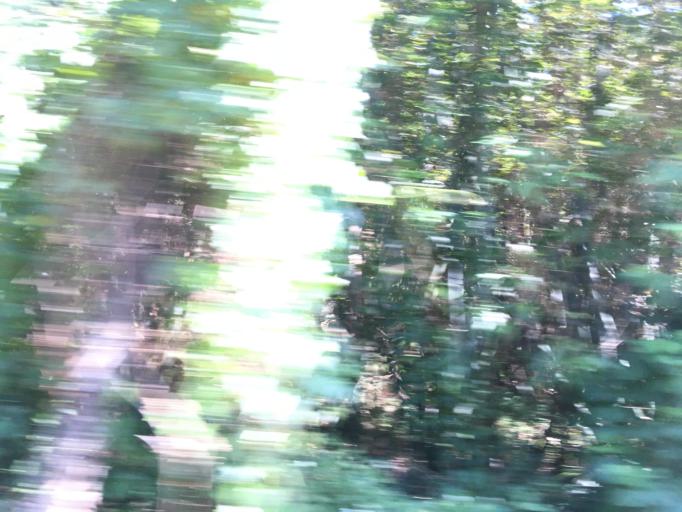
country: TW
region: Taipei
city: Taipei
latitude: 25.1532
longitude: 121.5027
